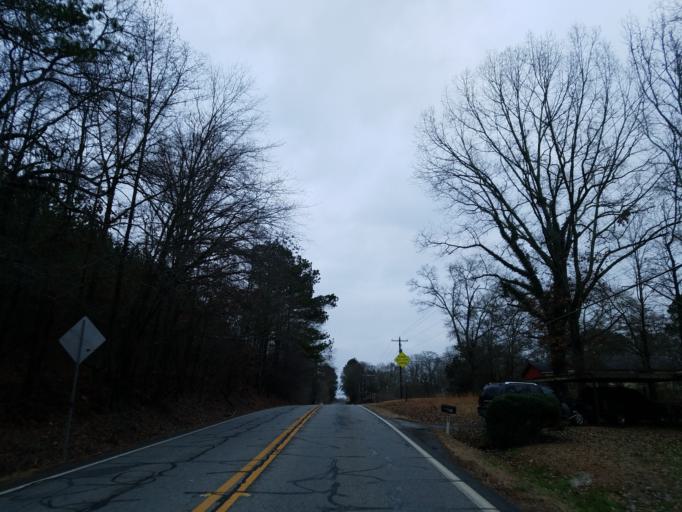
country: US
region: Georgia
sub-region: Bartow County
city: Cartersville
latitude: 34.2140
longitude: -84.8391
